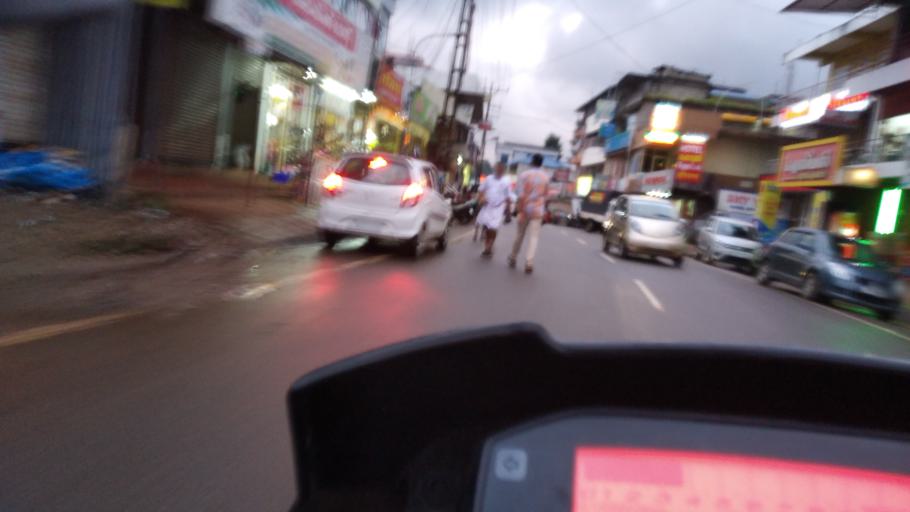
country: IN
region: Kerala
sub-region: Idukki
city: Munnar
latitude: 9.9633
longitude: 77.0979
